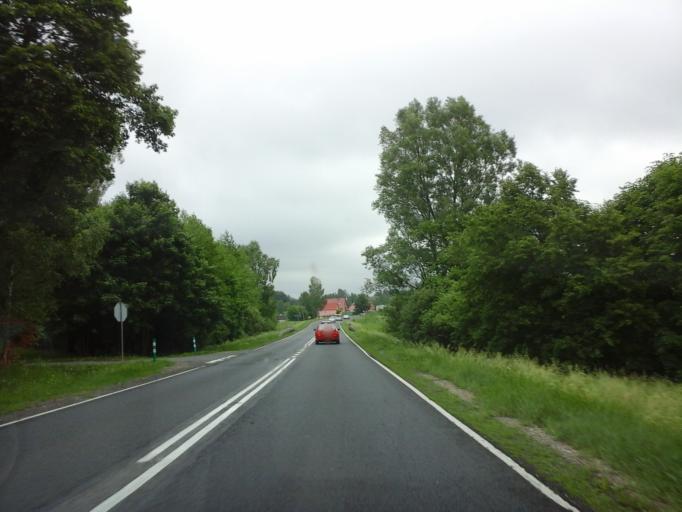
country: PL
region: West Pomeranian Voivodeship
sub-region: Powiat walecki
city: Miroslawiec
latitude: 53.3364
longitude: 16.0679
